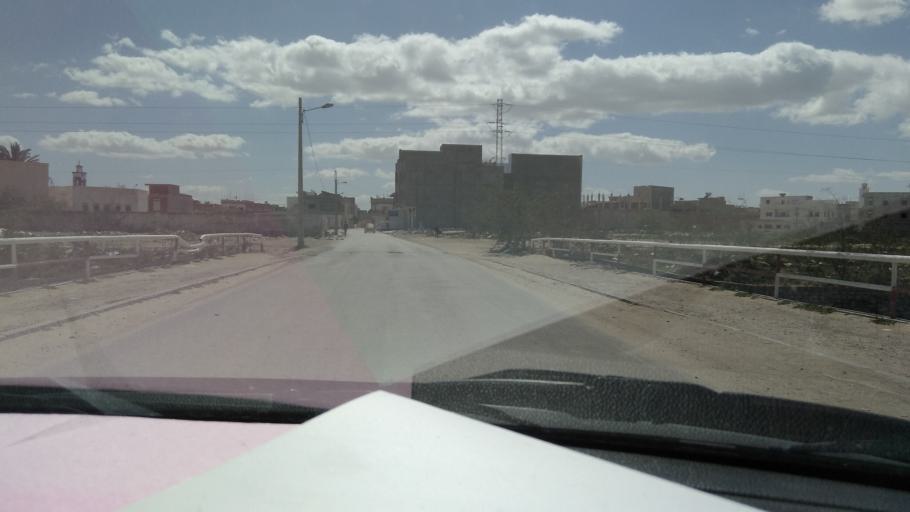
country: TN
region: Al Qayrawan
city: Kairouan
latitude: 35.6646
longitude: 10.1090
